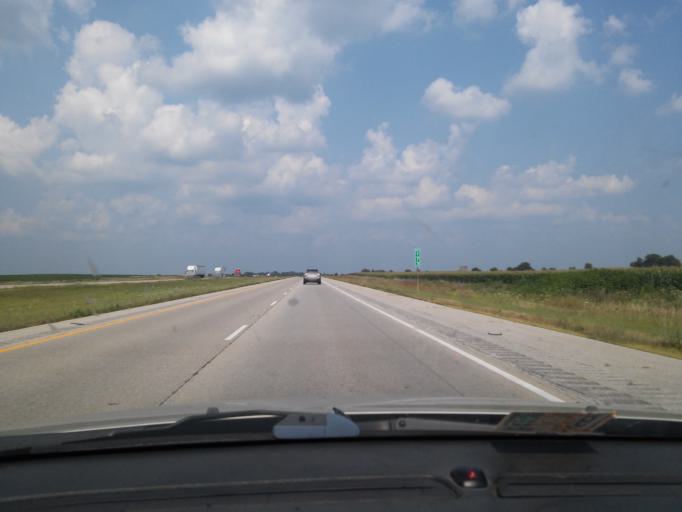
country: US
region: Illinois
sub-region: McLean County
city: Lexington
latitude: 40.5865
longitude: -88.8706
